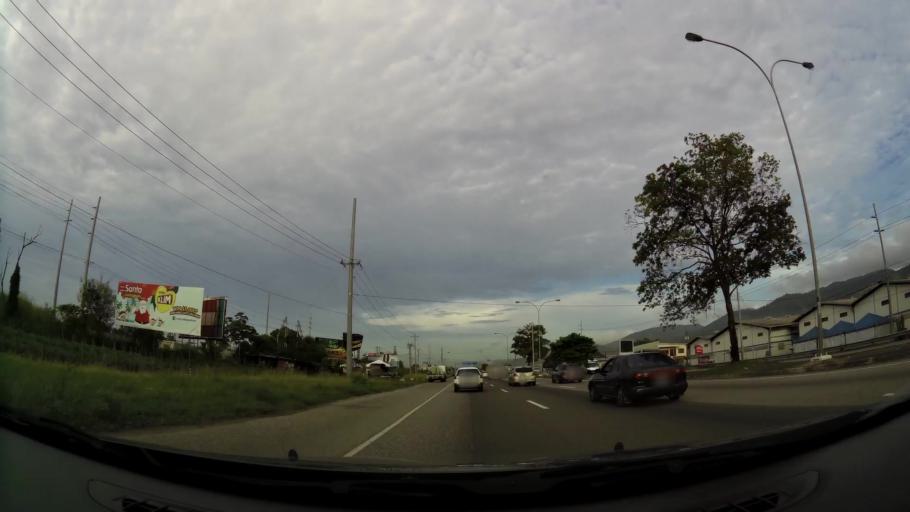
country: TT
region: Tunapuna/Piarco
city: Tunapuna
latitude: 10.6368
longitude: -61.3752
